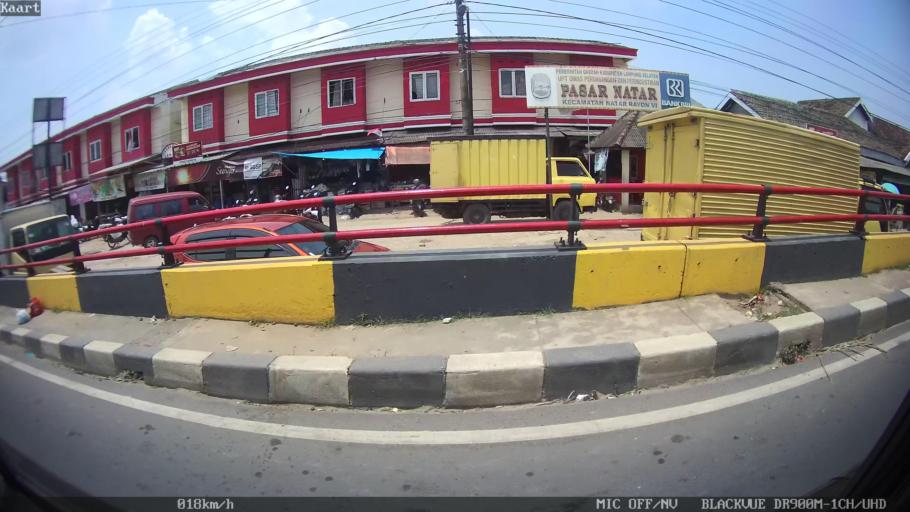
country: ID
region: Lampung
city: Natar
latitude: -5.3182
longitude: 105.1981
